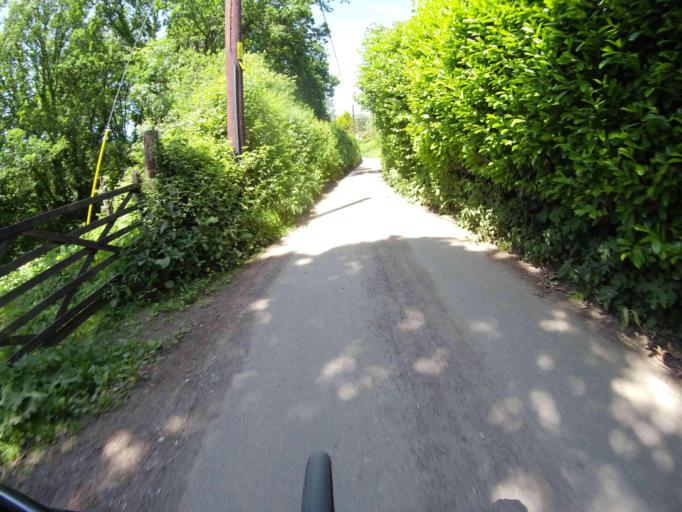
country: GB
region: England
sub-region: Devon
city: Bovey Tracey
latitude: 50.6079
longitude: -3.7083
